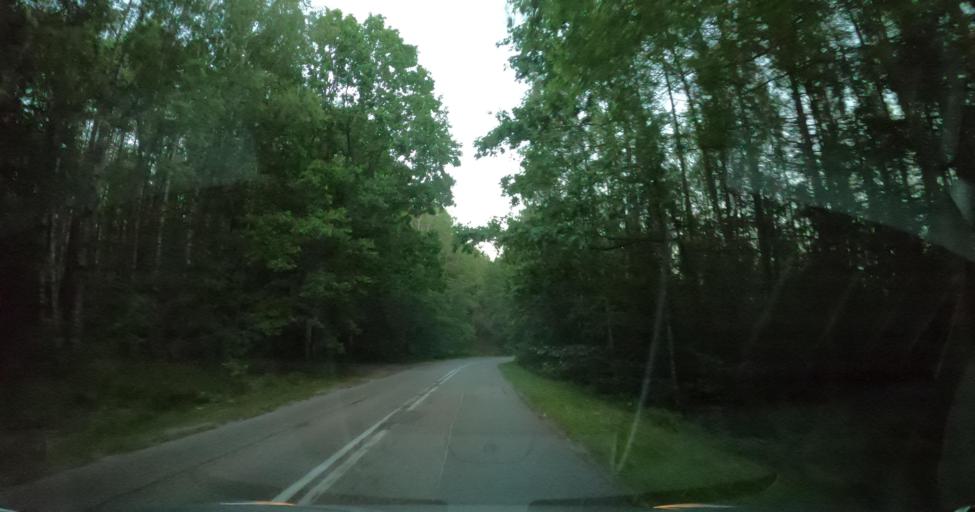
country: PL
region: Pomeranian Voivodeship
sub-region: Powiat wejherowski
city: Linia
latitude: 54.4611
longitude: 17.9993
